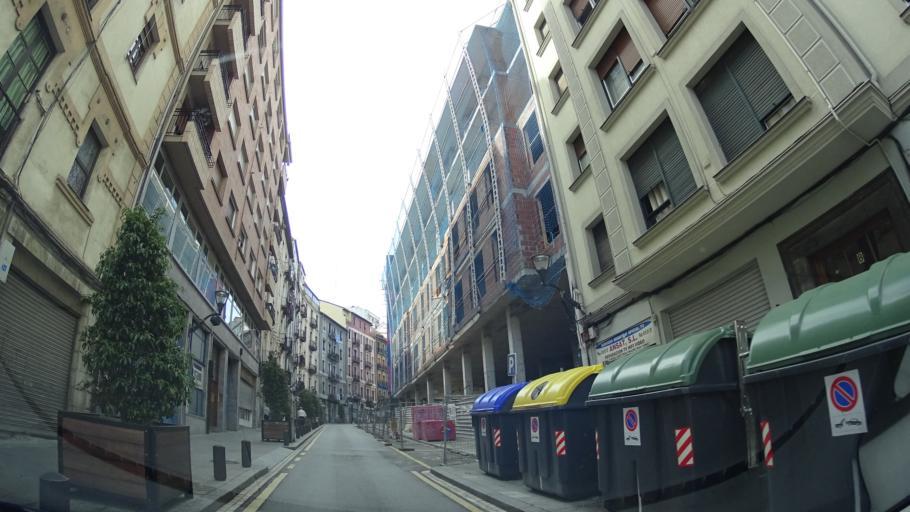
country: ES
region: Basque Country
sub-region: Bizkaia
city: Bilbao
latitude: 43.2558
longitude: -2.9317
